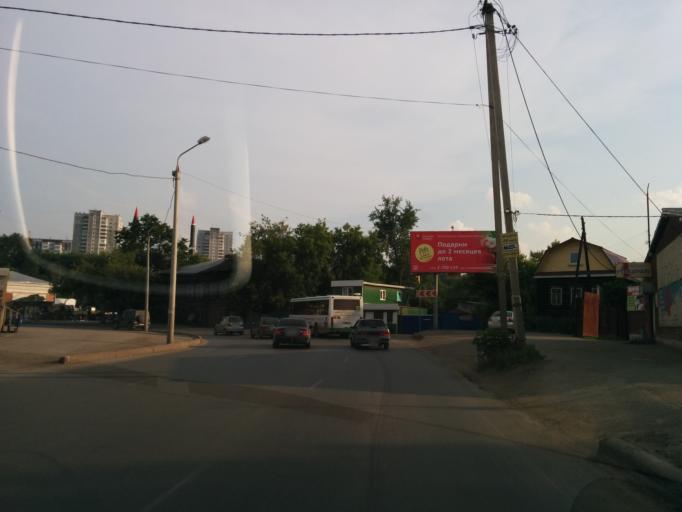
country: RU
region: Perm
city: Perm
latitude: 58.0371
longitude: 56.3095
